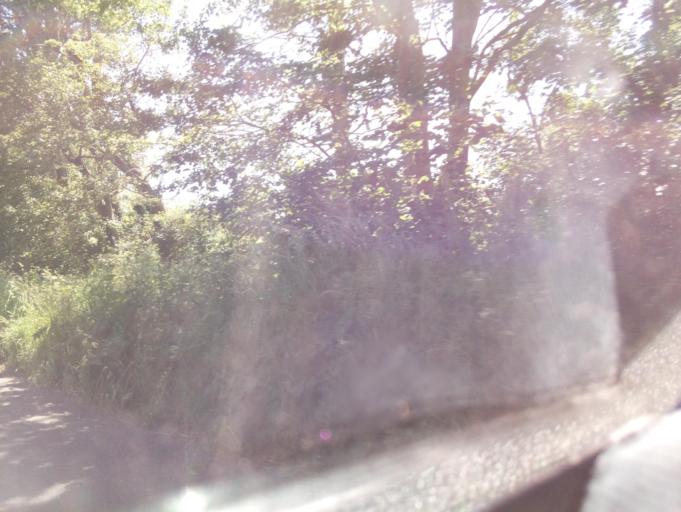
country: GB
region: England
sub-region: Wiltshire
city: Bremhill
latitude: 51.4752
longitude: -2.0621
